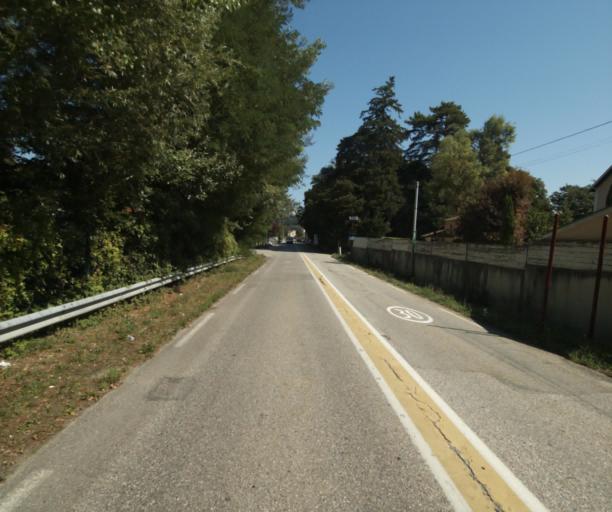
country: FR
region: Rhone-Alpes
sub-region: Departement de l'Isere
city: Allieres-et-Risset
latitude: 45.0836
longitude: 5.6814
